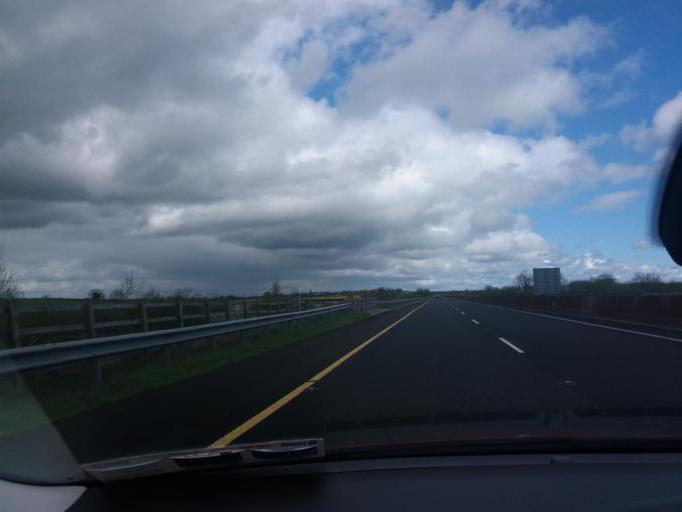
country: IE
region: Munster
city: Thurles
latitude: 52.6412
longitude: -7.7571
